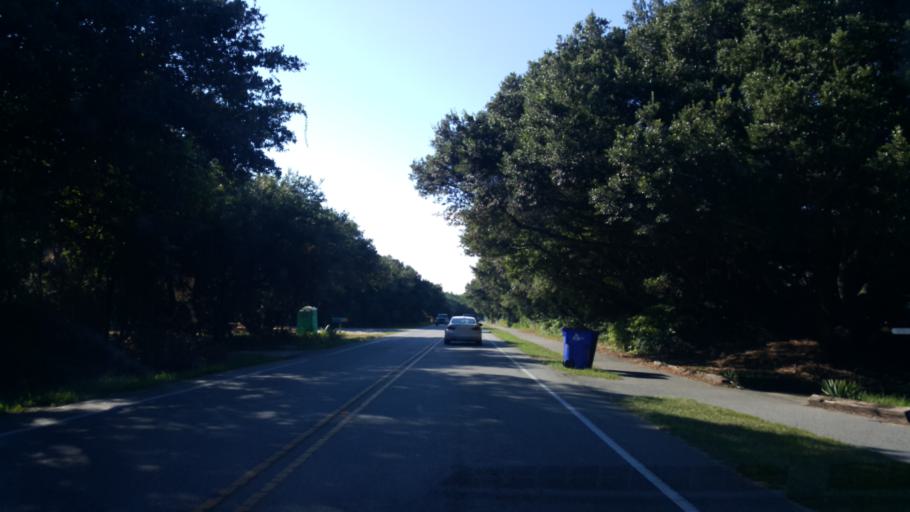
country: US
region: North Carolina
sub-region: Dare County
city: Southern Shores
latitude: 36.1312
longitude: -75.7321
